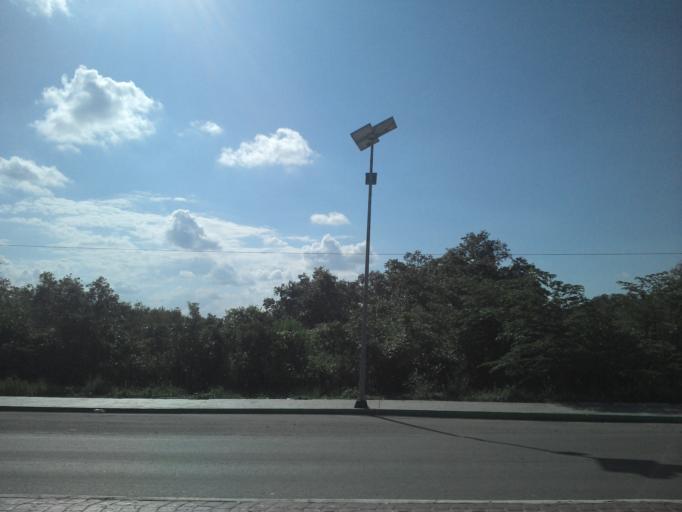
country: MX
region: Chiapas
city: Palenque
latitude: 17.5333
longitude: -91.9918
